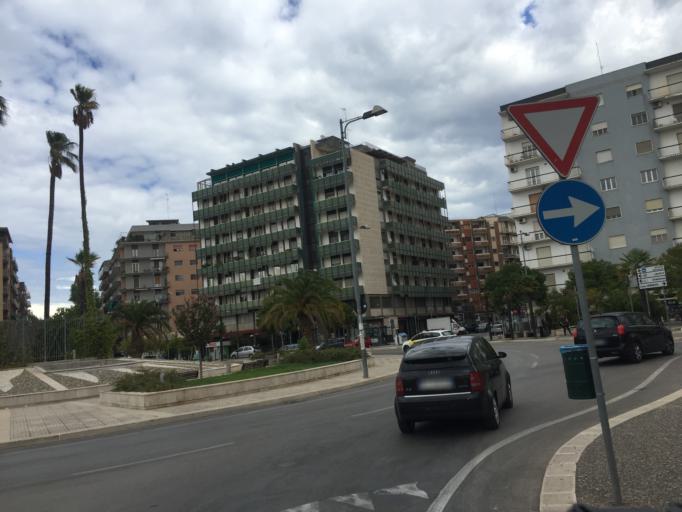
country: IT
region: Apulia
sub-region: Provincia di Bari
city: Bari
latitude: 41.1119
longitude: 16.8629
